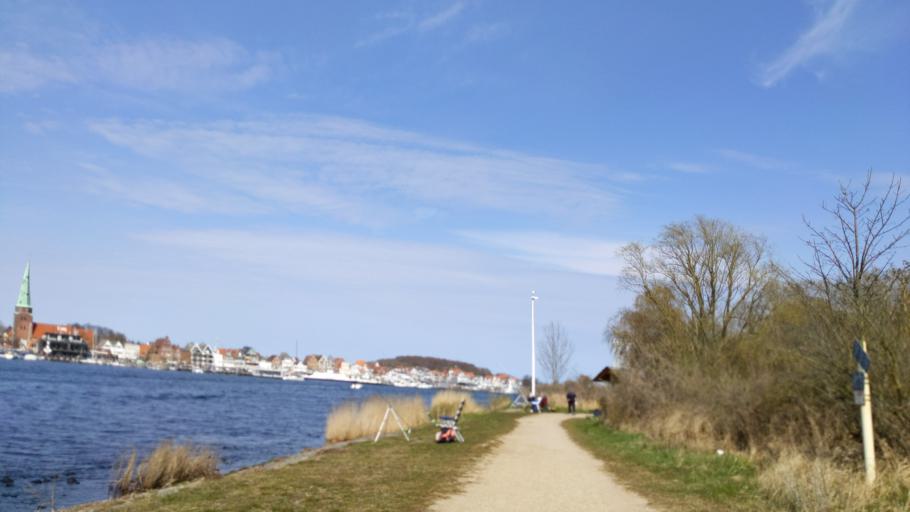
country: DE
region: Schleswig-Holstein
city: Travemuende
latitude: 53.9517
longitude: 10.8652
